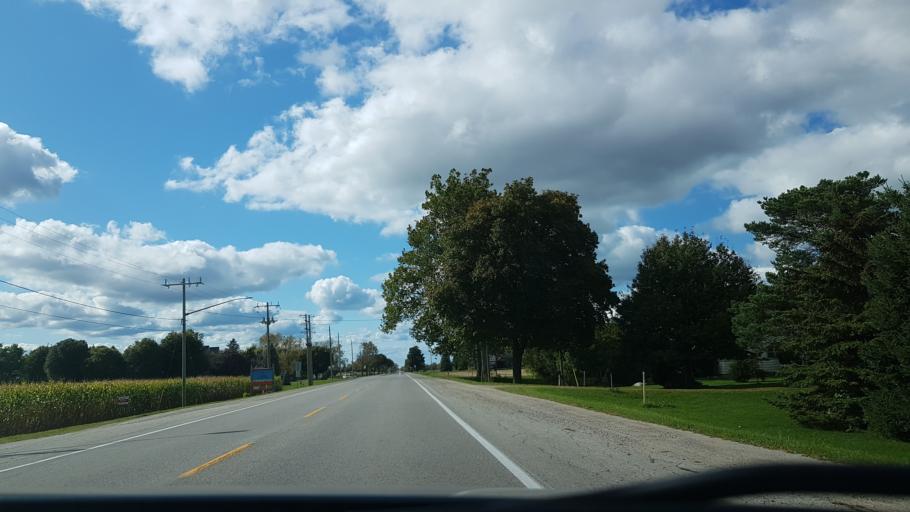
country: CA
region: Ontario
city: South Huron
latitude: 43.3456
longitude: -81.6400
